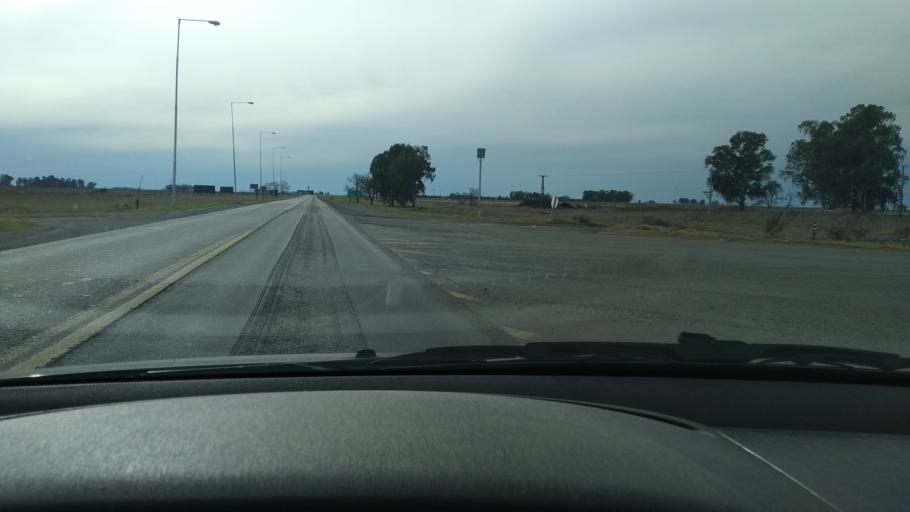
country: AR
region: Buenos Aires
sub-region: Partido de Azul
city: Azul
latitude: -36.7578
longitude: -59.8051
